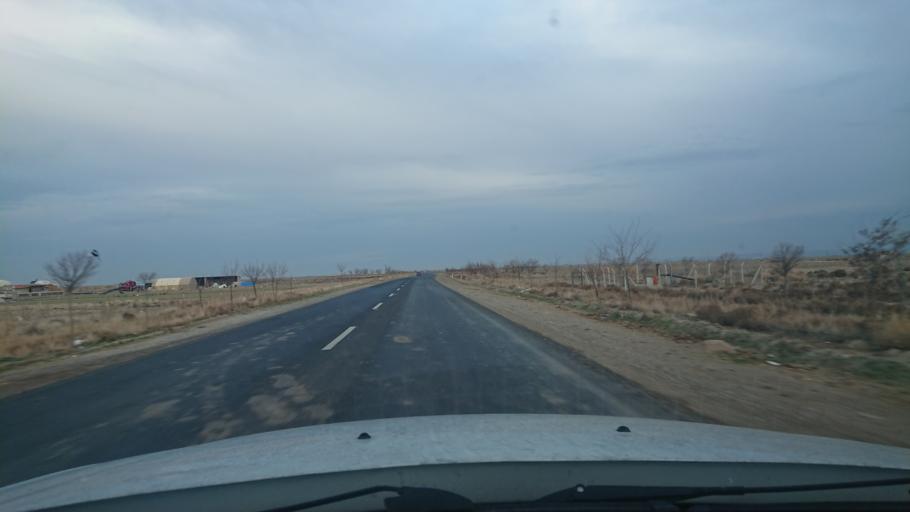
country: TR
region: Aksaray
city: Yesilova
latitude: 38.3070
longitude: 33.7550
